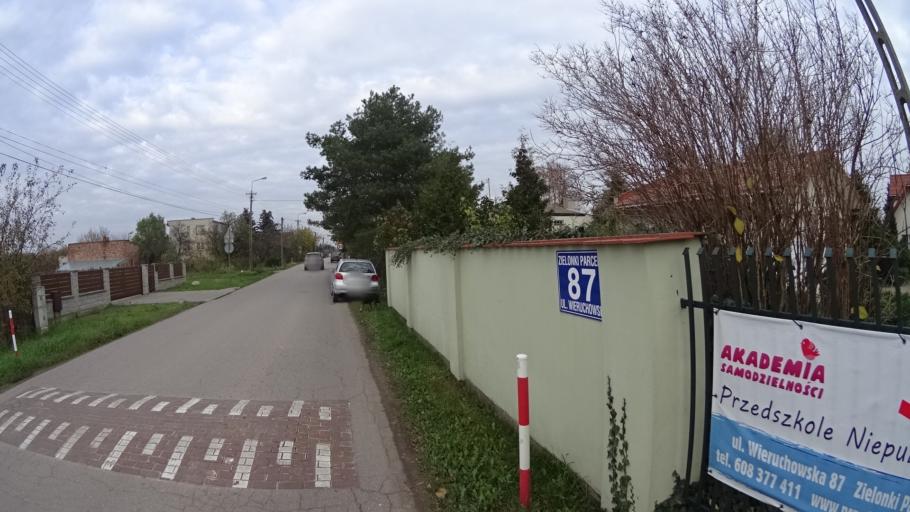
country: PL
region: Masovian Voivodeship
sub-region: Powiat warszawski zachodni
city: Stare Babice
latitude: 52.2394
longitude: 20.8289
